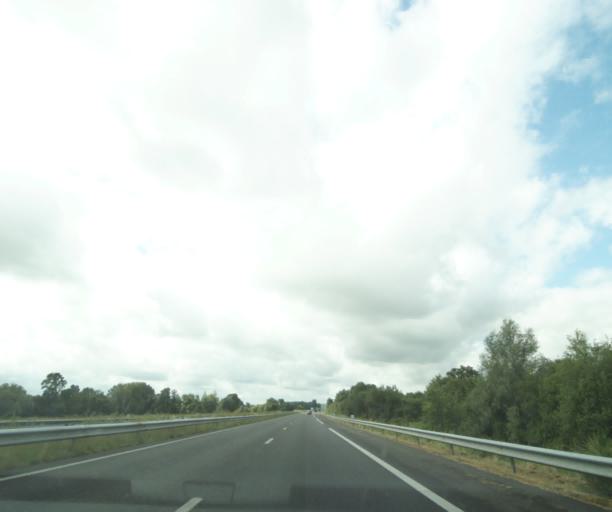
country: FR
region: Pays de la Loire
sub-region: Departement de Maine-et-Loire
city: Durtal
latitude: 47.6946
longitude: -0.2495
